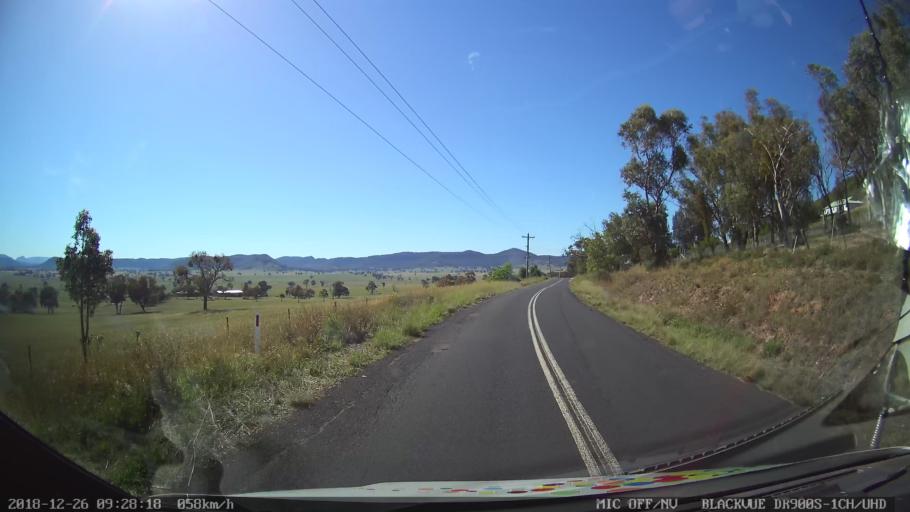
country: AU
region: New South Wales
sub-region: Mid-Western Regional
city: Kandos
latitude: -32.8434
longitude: 150.0214
